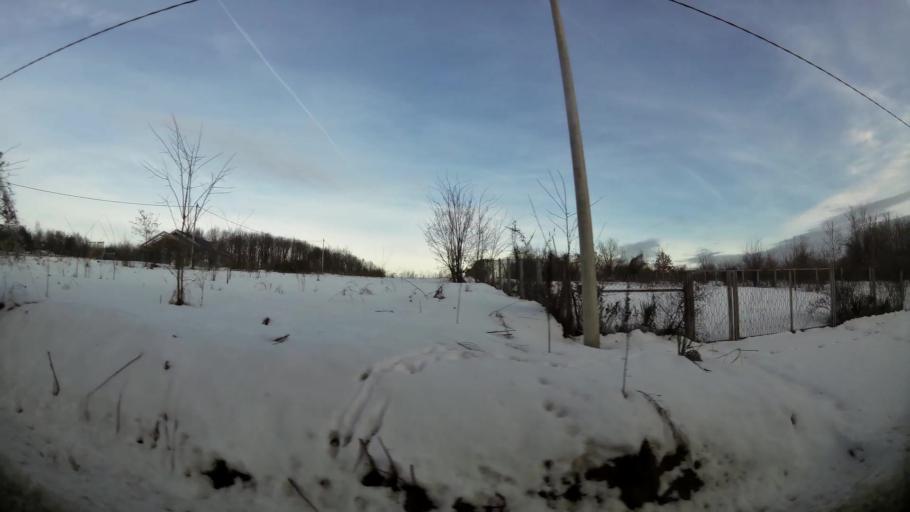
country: RS
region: Central Serbia
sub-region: Belgrade
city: Zvezdara
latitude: 44.7299
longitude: 20.5118
